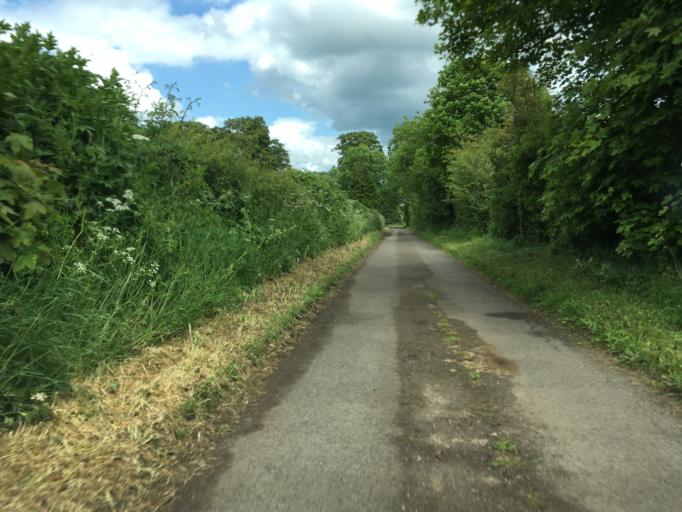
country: GB
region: England
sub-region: Gloucestershire
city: Cirencester
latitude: 51.7640
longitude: -1.9822
